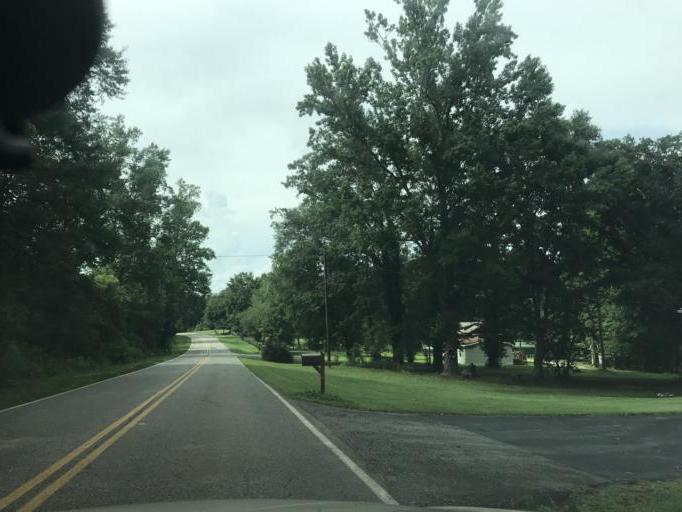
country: US
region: Georgia
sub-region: Forsyth County
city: Cumming
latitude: 34.2840
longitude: -84.2365
